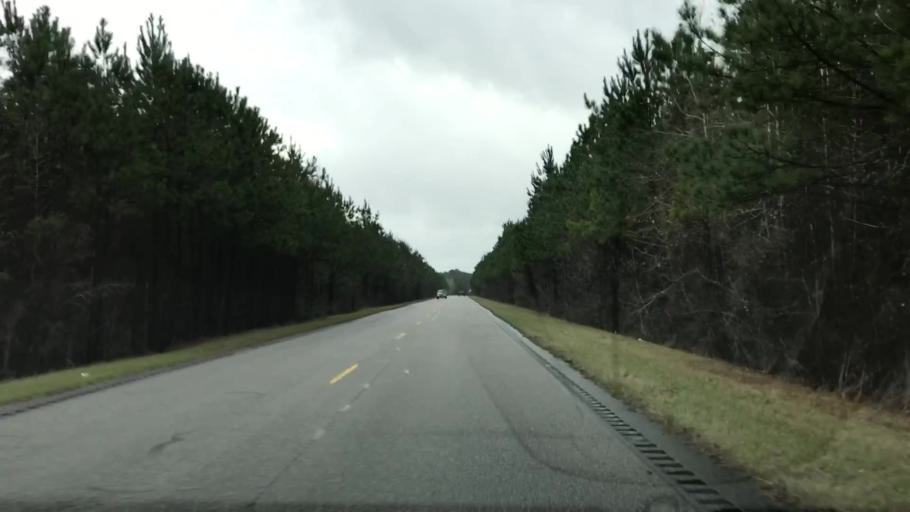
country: US
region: South Carolina
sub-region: Williamsburg County
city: Andrews
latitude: 33.5685
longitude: -79.4521
